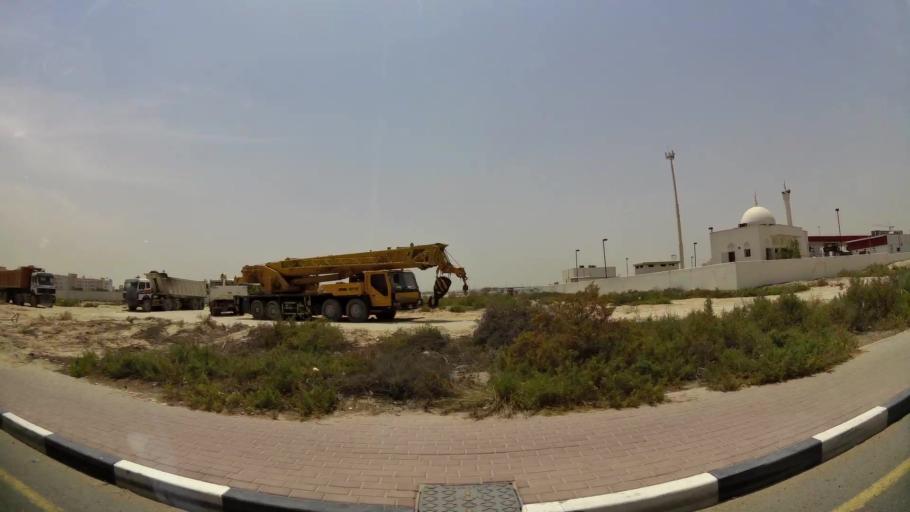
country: AE
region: Ash Shariqah
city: Sharjah
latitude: 25.1760
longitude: 55.4108
